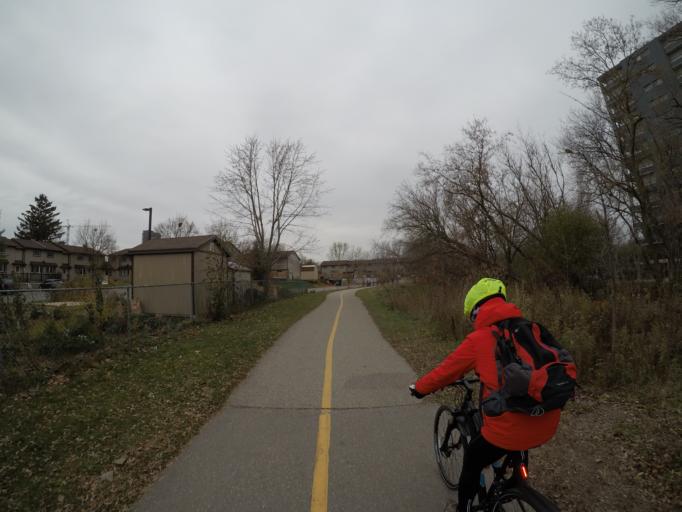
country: CA
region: Ontario
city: Waterloo
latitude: 43.4691
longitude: -80.5185
